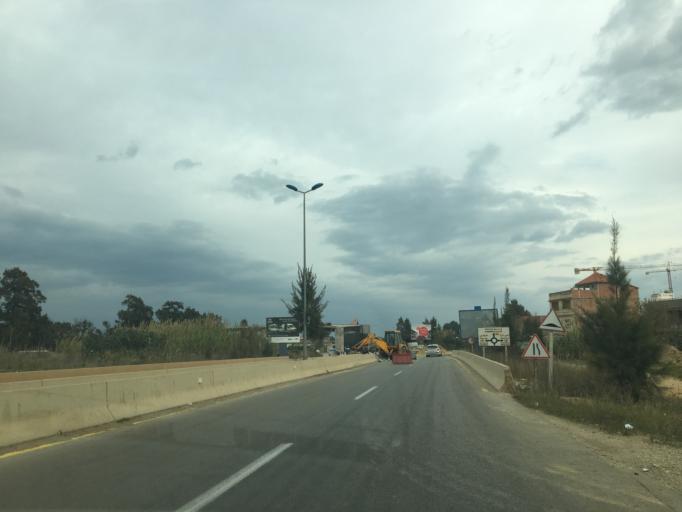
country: DZ
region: Tipaza
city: Tipasa
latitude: 36.5854
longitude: 2.4265
